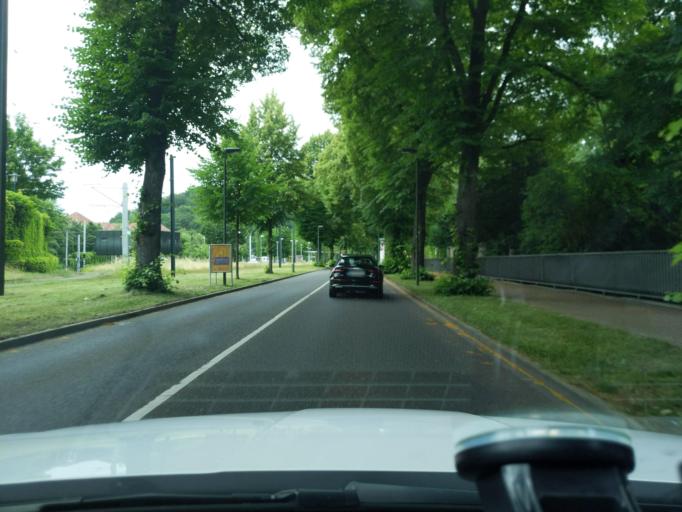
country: DE
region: North Rhine-Westphalia
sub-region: Regierungsbezirk Dusseldorf
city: Ratingen
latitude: 51.2439
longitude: 6.8526
